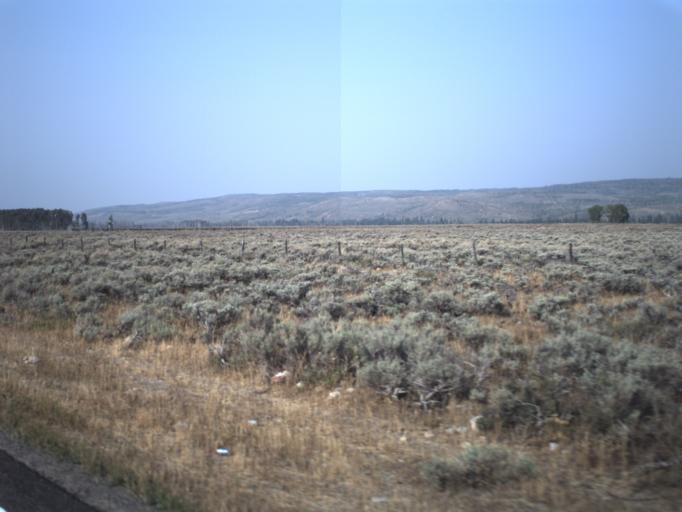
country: US
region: Wyoming
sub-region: Uinta County
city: Evanston
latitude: 40.9564
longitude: -110.8432
